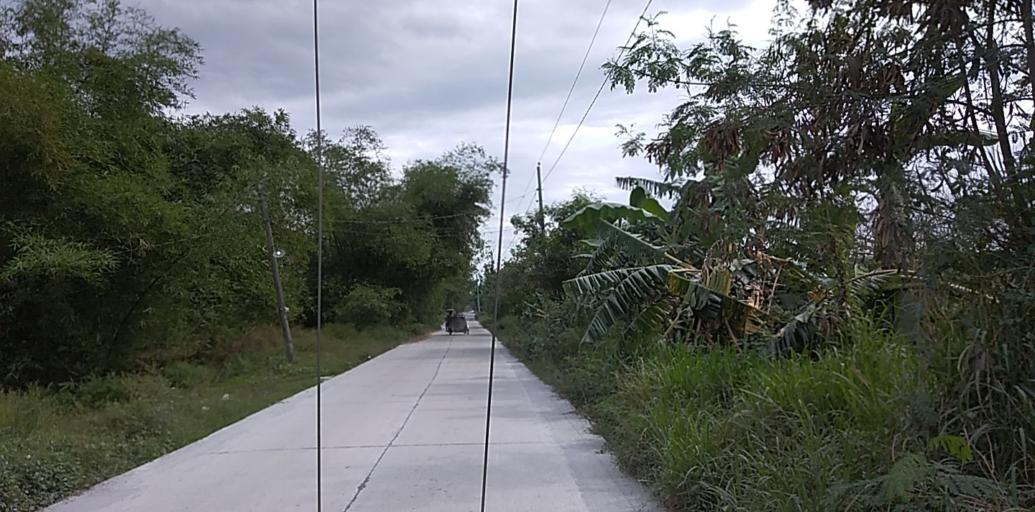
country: PH
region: Central Luzon
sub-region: Province of Pampanga
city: Pulung Santol
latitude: 15.0559
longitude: 120.5583
